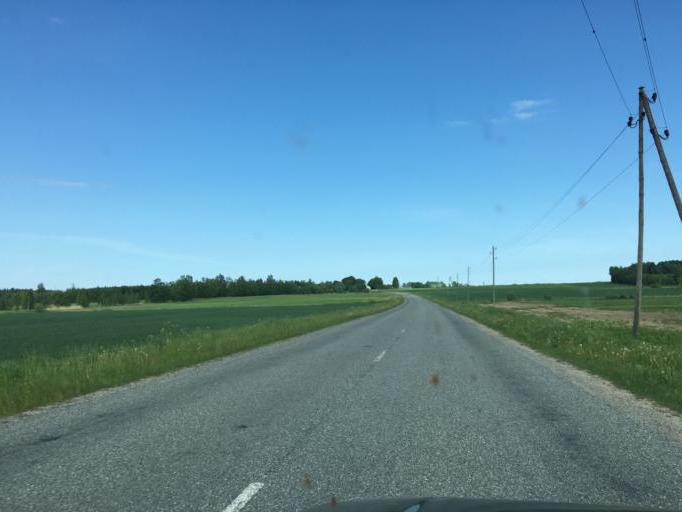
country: LV
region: Talsu Rajons
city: Valdemarpils
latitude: 57.3672
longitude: 22.4870
